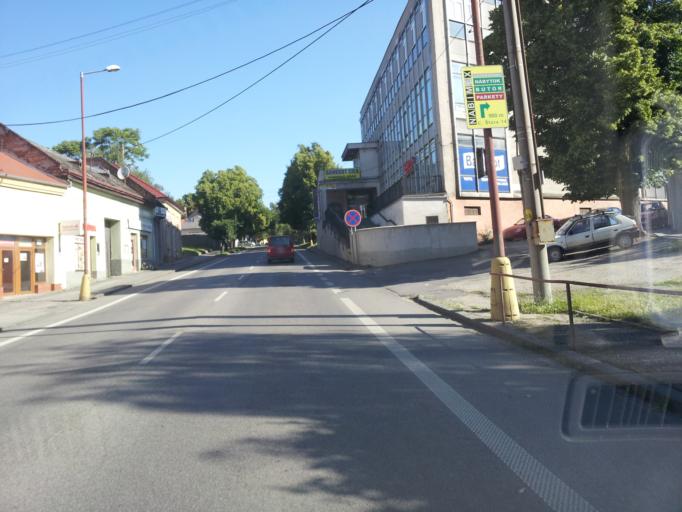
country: SK
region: Nitriansky
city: Sahy
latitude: 48.0708
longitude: 18.9476
